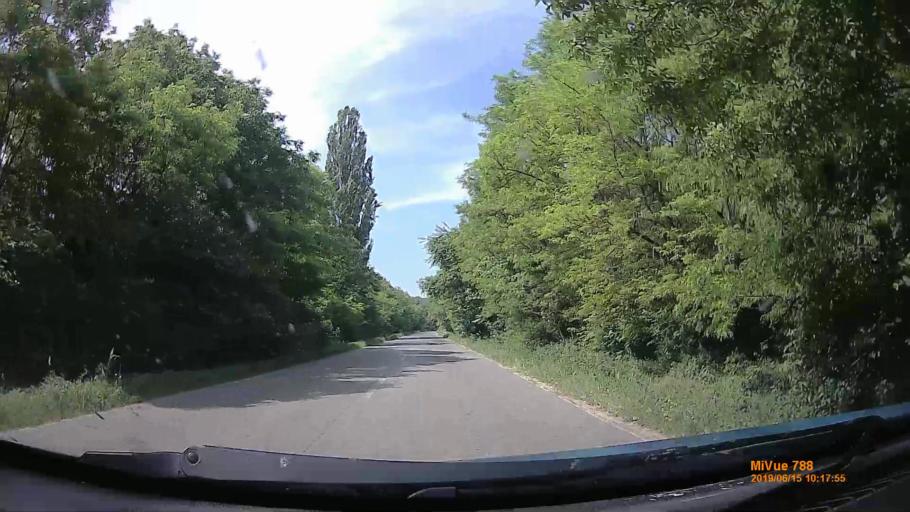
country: HU
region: Baranya
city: Buekkoesd
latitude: 46.1219
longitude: 18.0001
